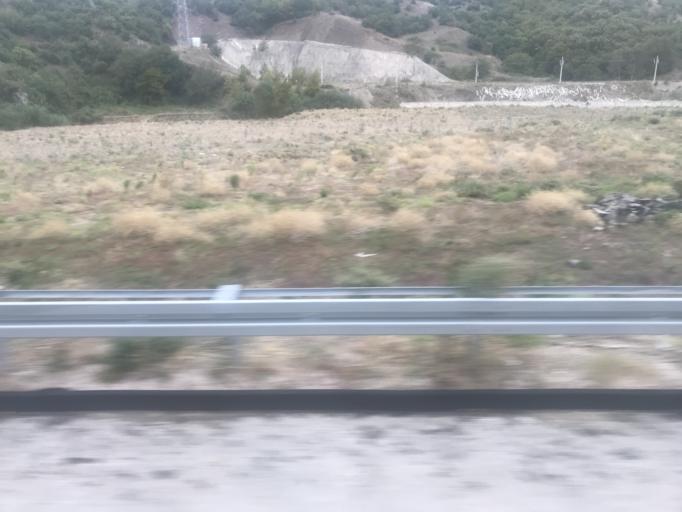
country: TR
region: Balikesir
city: Susurluk
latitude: 39.8970
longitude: 28.1061
